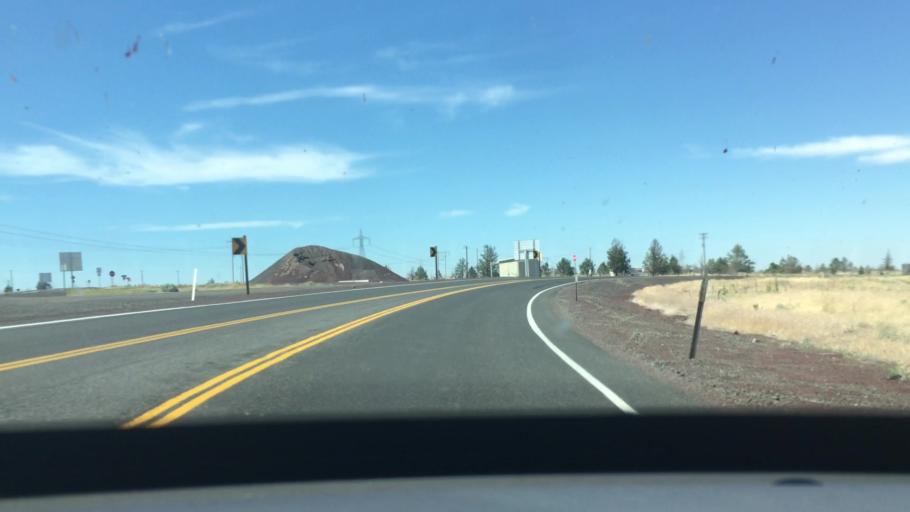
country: US
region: Oregon
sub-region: Jefferson County
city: Madras
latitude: 44.9203
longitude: -120.9457
